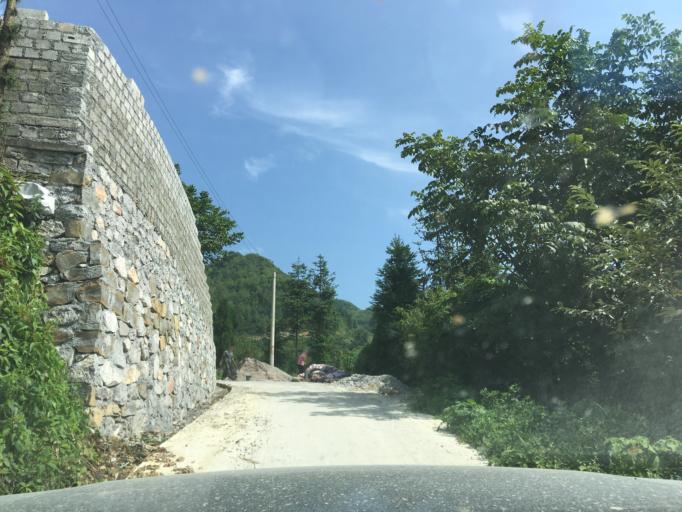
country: CN
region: Guangxi Zhuangzu Zizhiqu
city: Xinzhou
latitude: 24.9651
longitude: 105.6208
